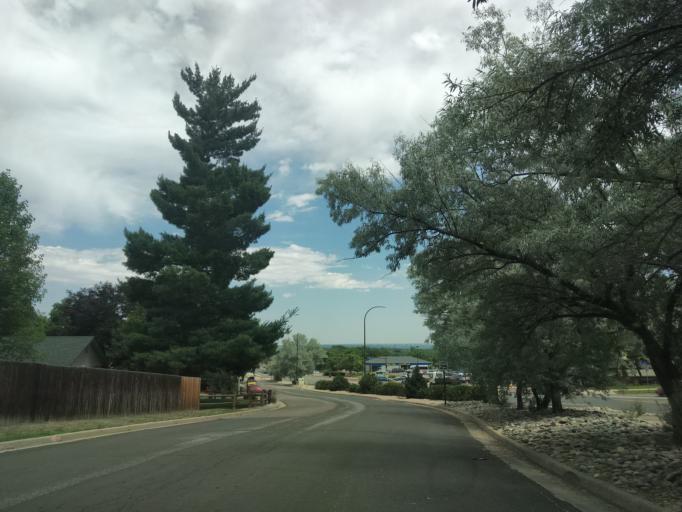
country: US
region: Colorado
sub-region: Jefferson County
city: Lakewood
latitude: 39.6824
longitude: -105.1239
